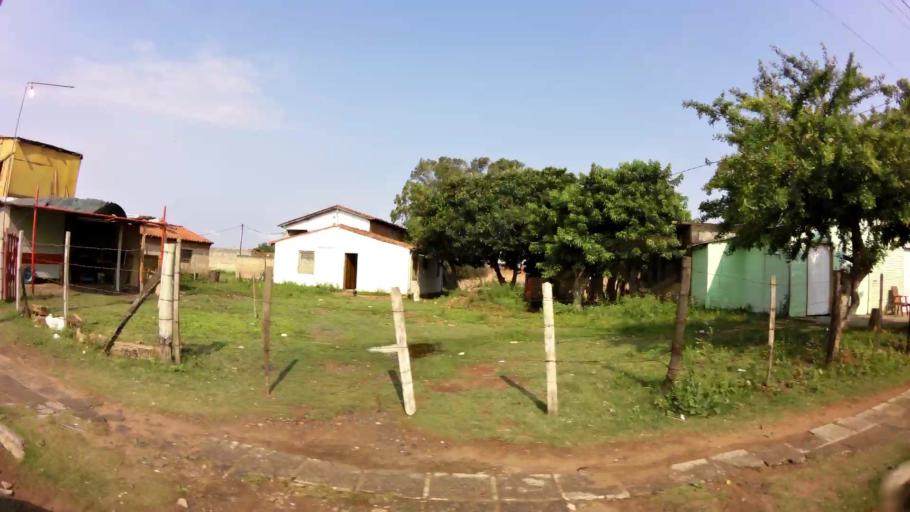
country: PY
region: Asuncion
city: Asuncion
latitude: -25.3080
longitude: -57.6674
